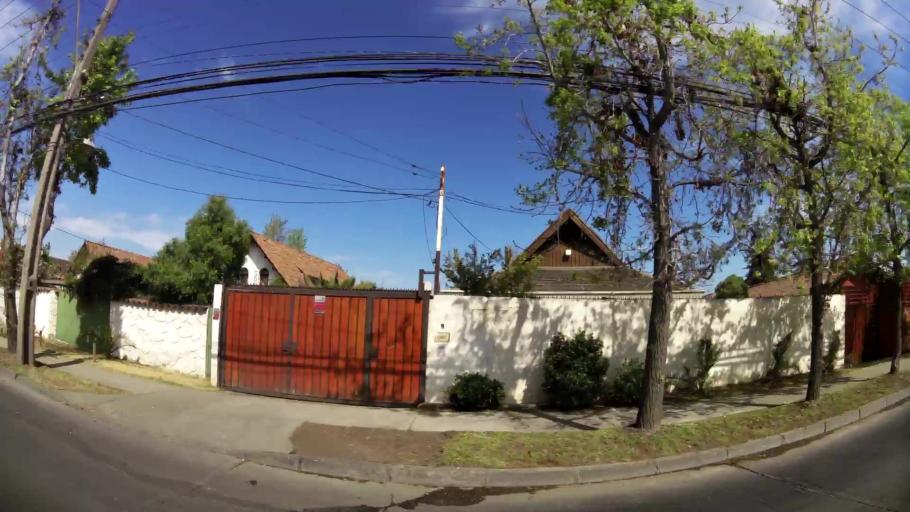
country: CL
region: Santiago Metropolitan
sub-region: Provincia de Santiago
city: Villa Presidente Frei, Nunoa, Santiago, Chile
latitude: -33.4384
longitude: -70.5364
